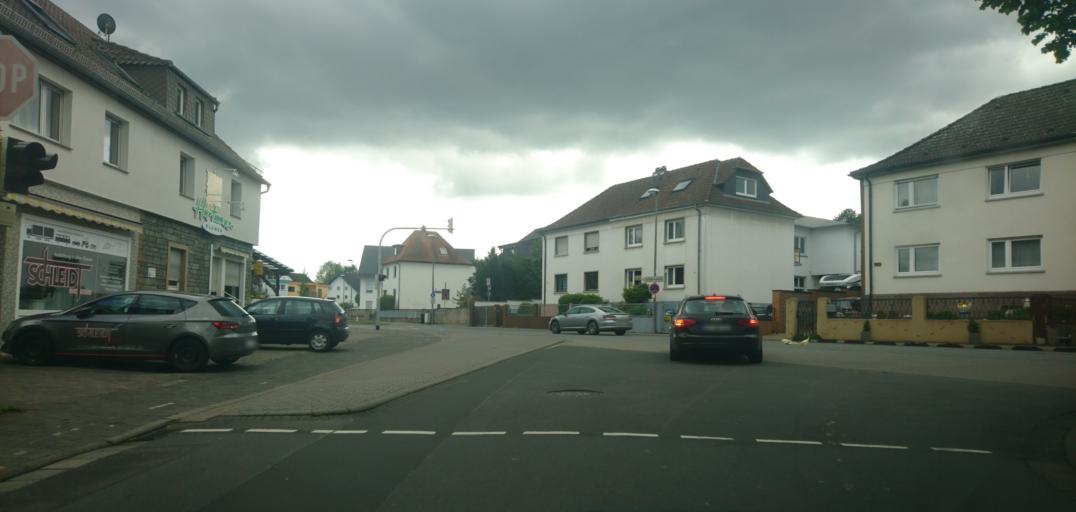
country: DE
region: Hesse
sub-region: Regierungsbezirk Darmstadt
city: Dietzenbach
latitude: 50.0049
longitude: 8.7754
